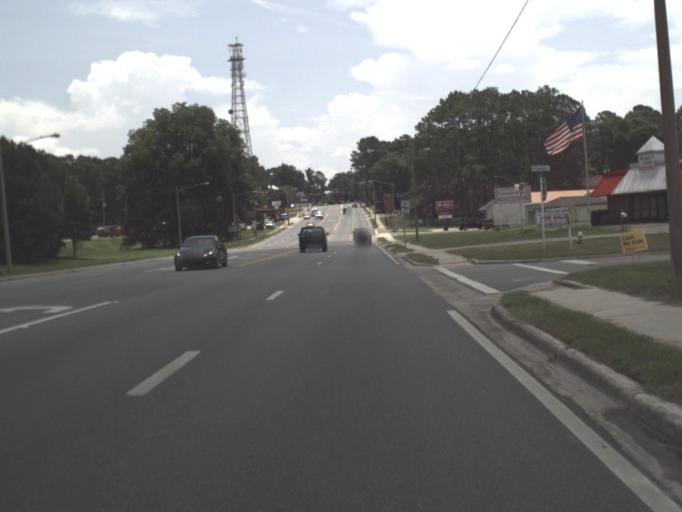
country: US
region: Florida
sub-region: Madison County
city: Madison
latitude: 30.4713
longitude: -83.4249
